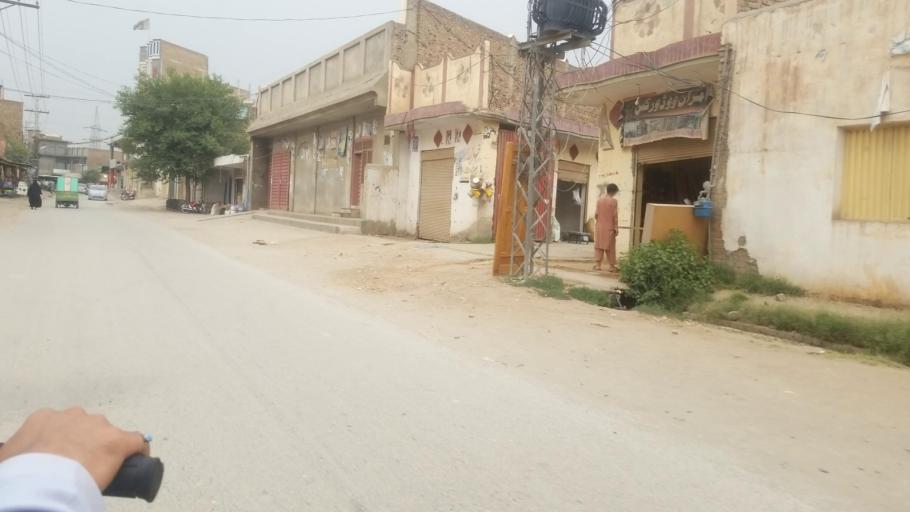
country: PK
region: Khyber Pakhtunkhwa
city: Peshawar
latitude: 33.9840
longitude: 71.5574
